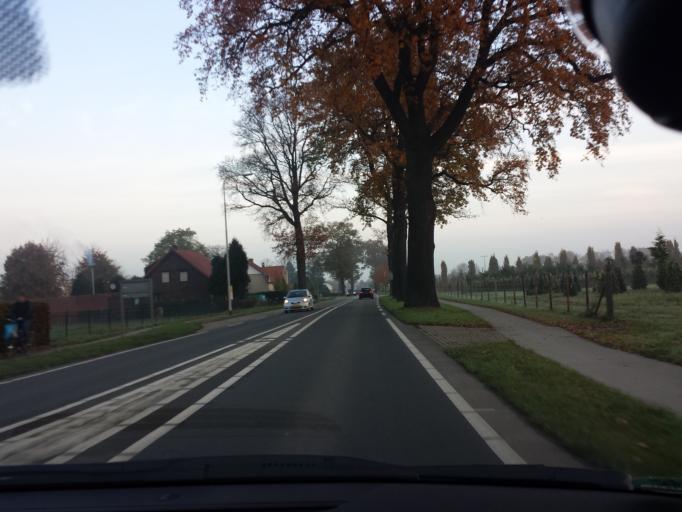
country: NL
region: Limburg
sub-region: Gemeente Maasgouw
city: Maasbracht
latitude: 51.0894
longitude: 5.8796
